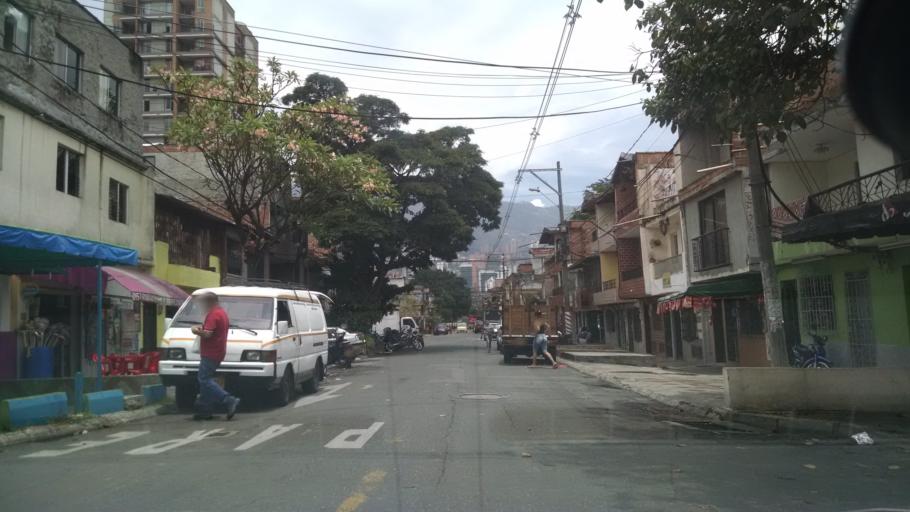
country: CO
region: Antioquia
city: Itagui
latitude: 6.2052
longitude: -75.5844
